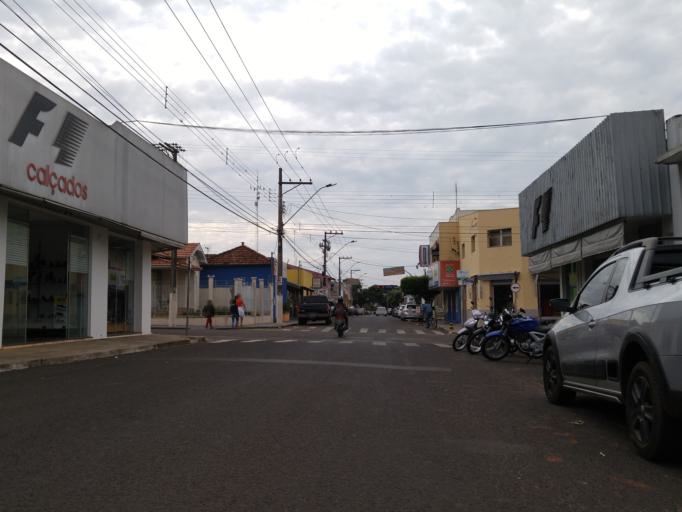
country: BR
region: Sao Paulo
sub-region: Paraguacu Paulista
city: Paraguacu Paulista
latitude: -22.4148
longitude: -50.5772
